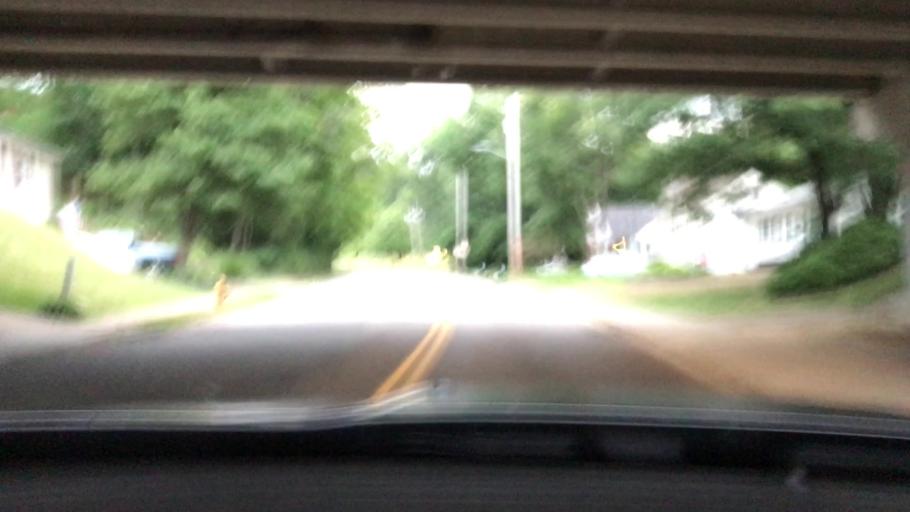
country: US
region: Iowa
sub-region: Scott County
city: Bettendorf
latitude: 41.5383
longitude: -90.5407
